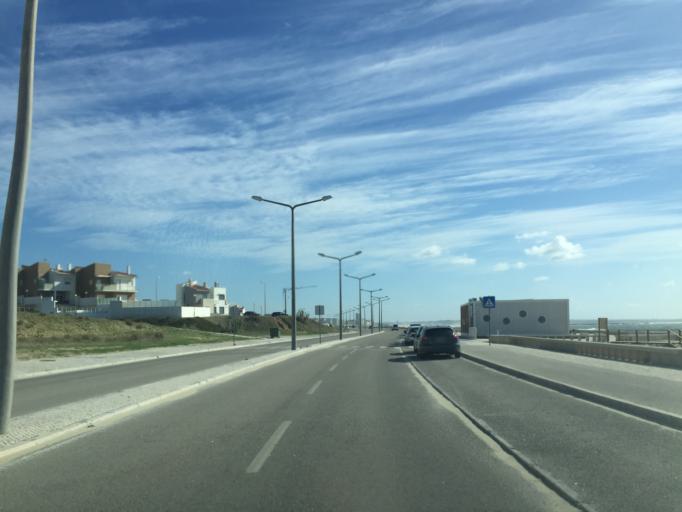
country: PT
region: Coimbra
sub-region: Figueira da Foz
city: Buarcos
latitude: 40.1698
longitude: -8.8886
